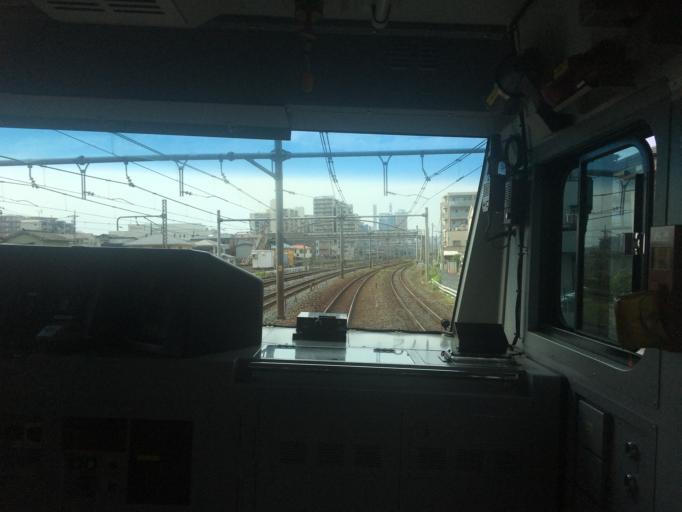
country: JP
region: Saitama
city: Yono
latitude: 35.8749
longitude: 139.6436
